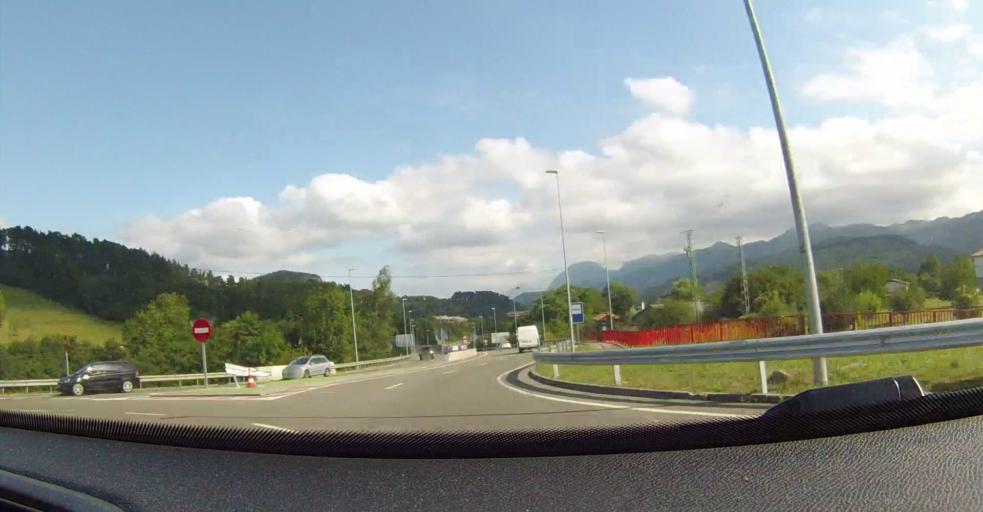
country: ES
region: Basque Country
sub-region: Bizkaia
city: Amorebieta
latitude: 43.2264
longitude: -2.7307
